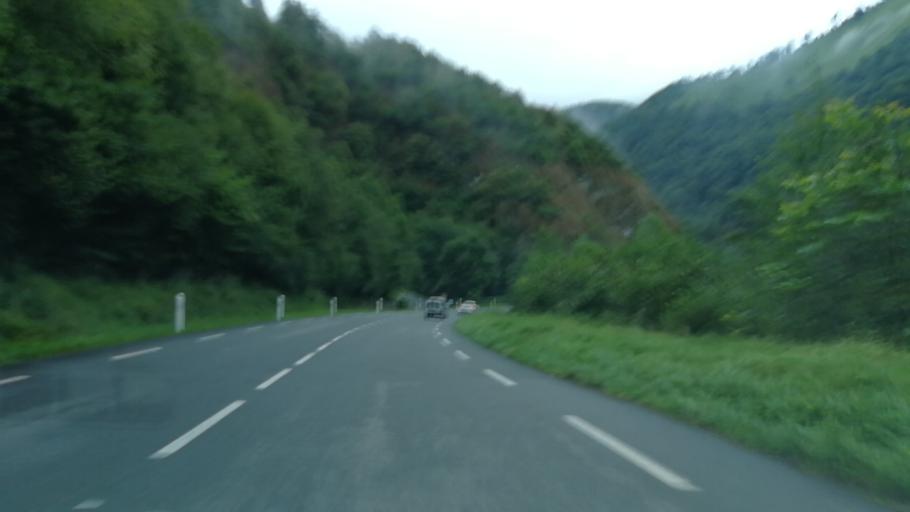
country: FR
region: Aquitaine
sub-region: Departement des Pyrenees-Atlantiques
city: Arette
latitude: 43.0390
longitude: -0.6053
